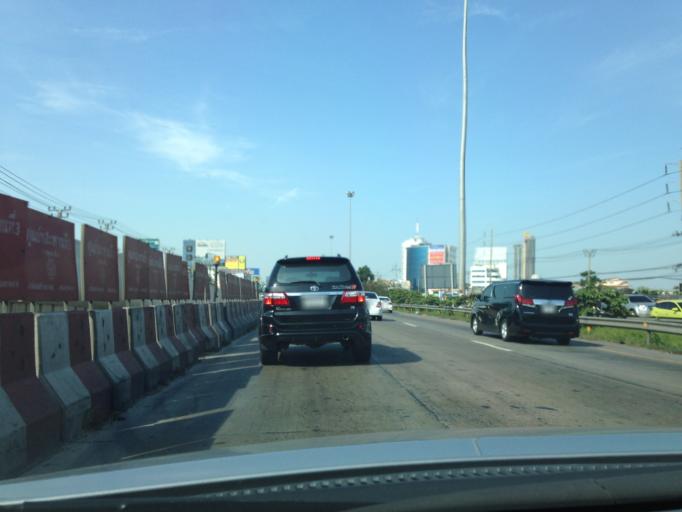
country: TH
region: Nonthaburi
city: Bang Bua Thong
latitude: 13.8649
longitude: 100.4107
